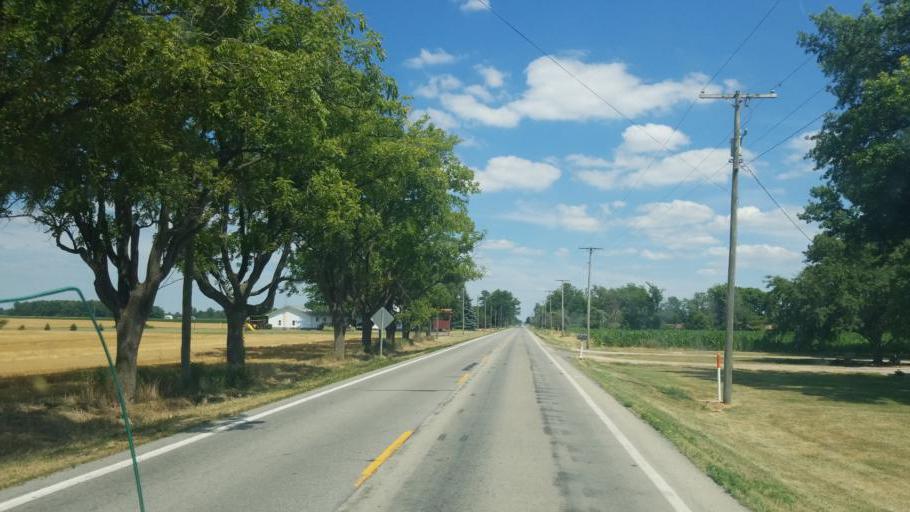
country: US
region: Ohio
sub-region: Defiance County
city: Hicksville
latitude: 41.2959
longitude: -84.7448
